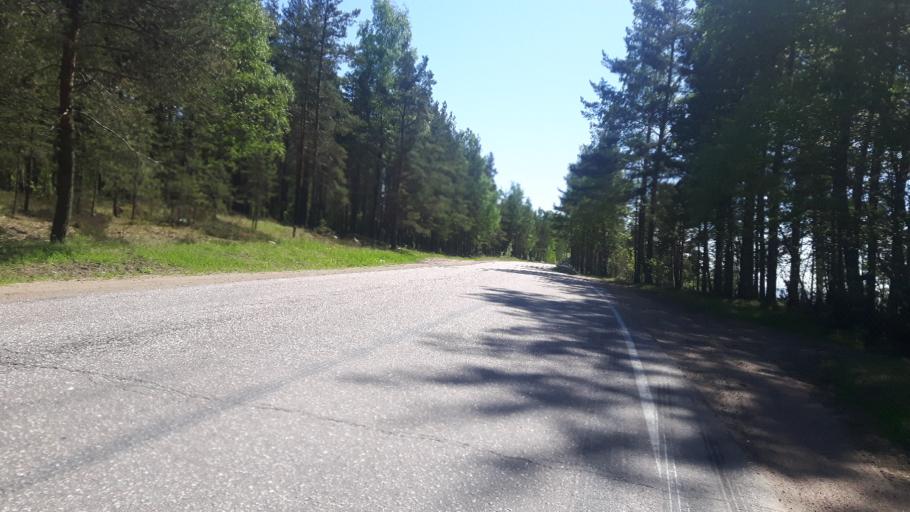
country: RU
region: Leningrad
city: Glebychevo
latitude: 60.3274
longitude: 28.8236
